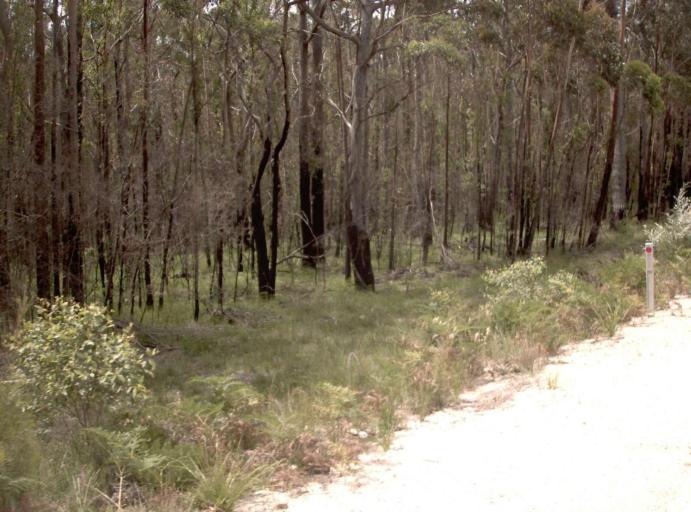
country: AU
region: New South Wales
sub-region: Bega Valley
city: Eden
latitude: -37.5333
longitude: 149.4843
